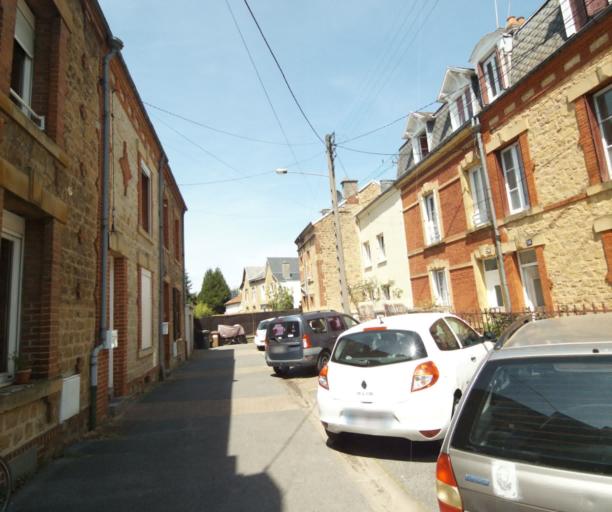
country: FR
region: Champagne-Ardenne
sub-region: Departement des Ardennes
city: Charleville-Mezieres
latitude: 49.7641
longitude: 4.7234
